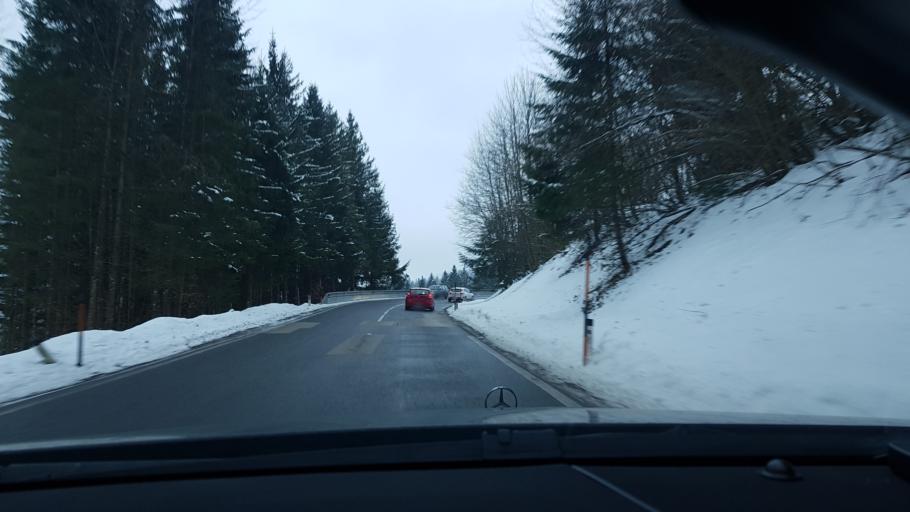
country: AT
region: Lower Austria
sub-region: Politischer Bezirk Scheibbs
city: Lunz am See
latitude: 47.8788
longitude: 15.0710
